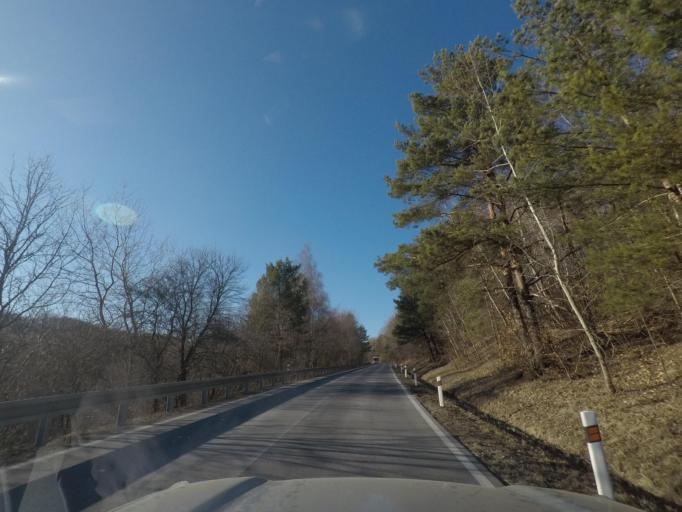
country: SK
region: Presovsky
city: Medzilaborce
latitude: 49.2730
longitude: 21.8634
